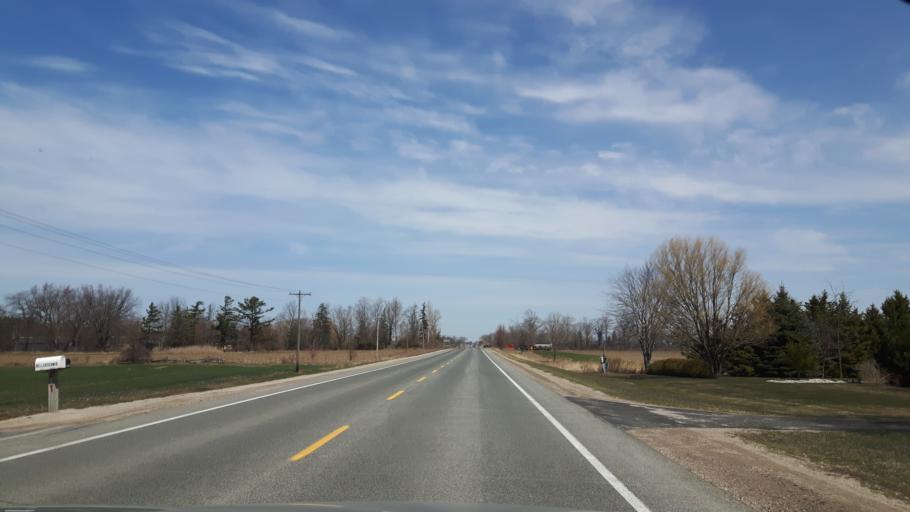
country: CA
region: Ontario
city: Goderich
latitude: 43.7120
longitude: -81.7056
